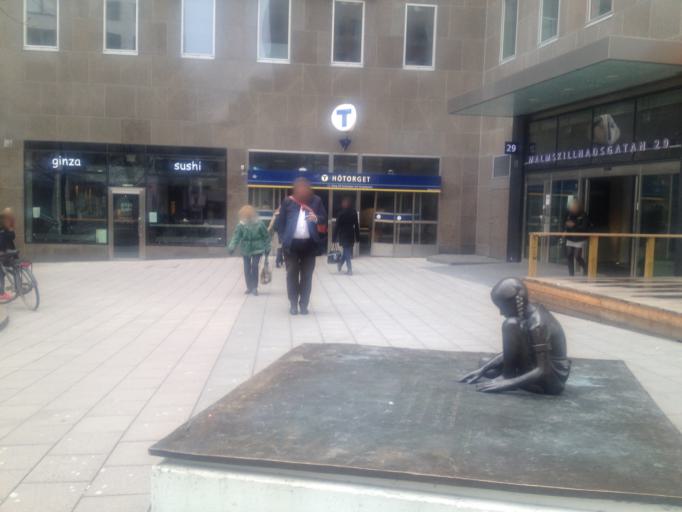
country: SE
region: Stockholm
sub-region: Stockholms Kommun
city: Stockholm
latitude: 59.3346
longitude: 18.0659
